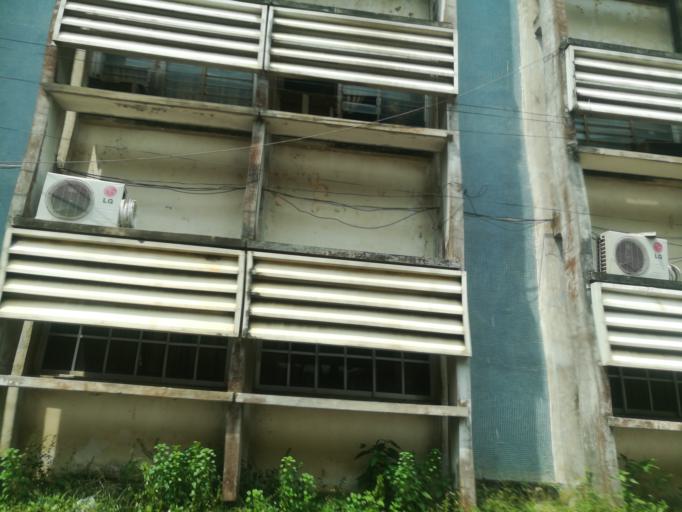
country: NG
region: Oyo
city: Ibadan
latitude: 7.4098
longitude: 3.9053
